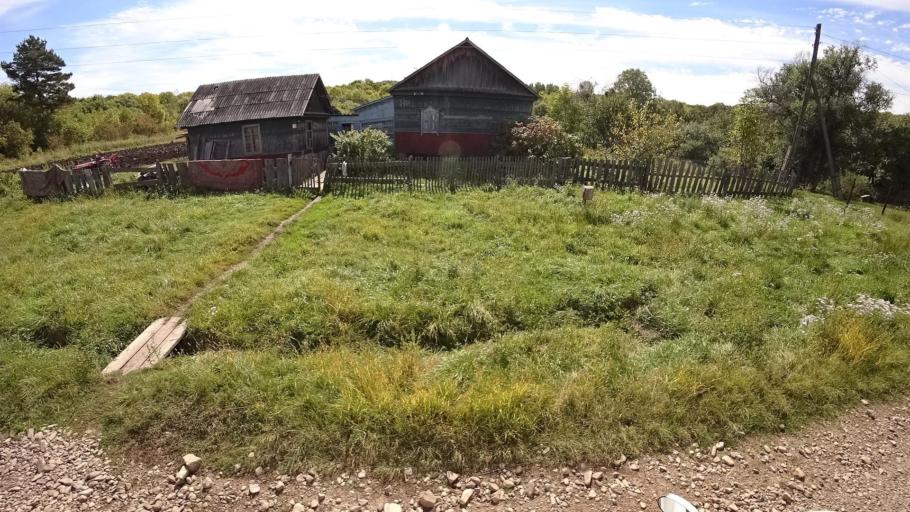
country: RU
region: Primorskiy
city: Kirovskiy
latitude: 44.7566
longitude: 133.6165
